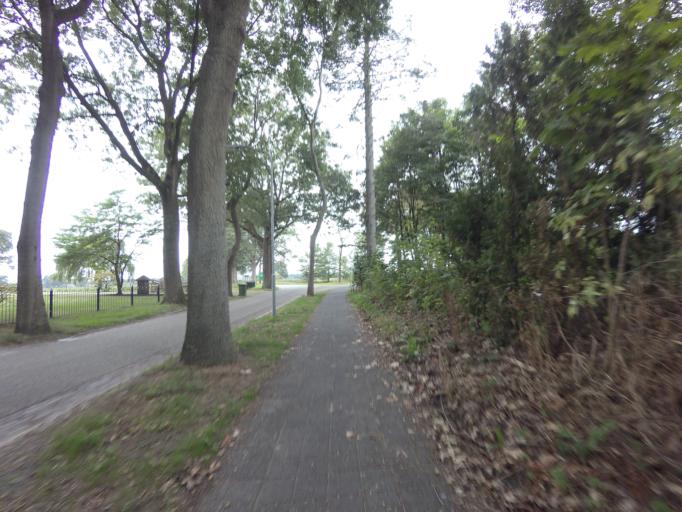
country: NL
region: Drenthe
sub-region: Gemeente Assen
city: Assen
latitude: 52.9913
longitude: 6.6399
